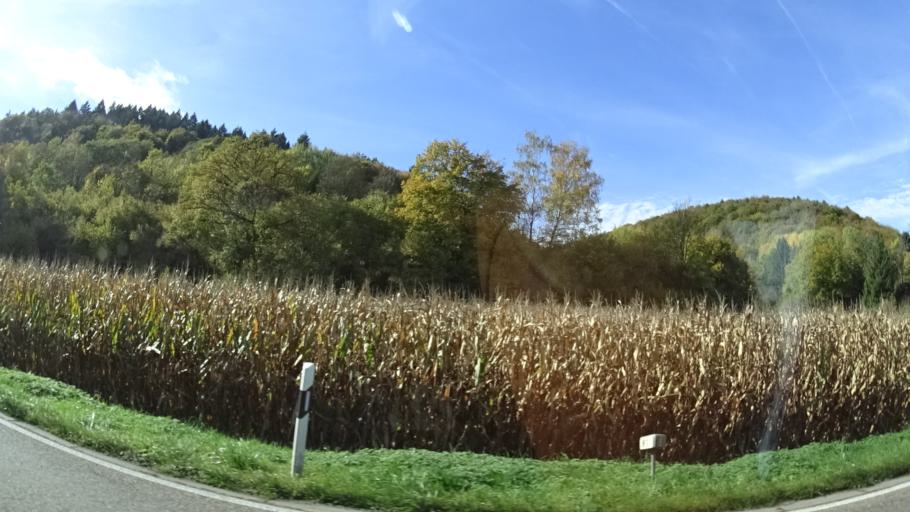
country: DE
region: Baden-Wuerttemberg
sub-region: Karlsruhe Region
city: Joehlingen
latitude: 48.9961
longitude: 8.5337
